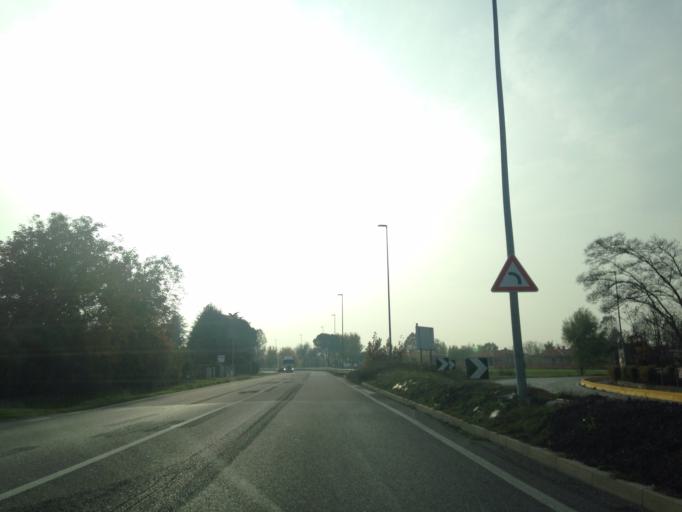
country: IT
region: Veneto
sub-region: Provincia di Treviso
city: Mansue
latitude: 45.8199
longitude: 12.5285
